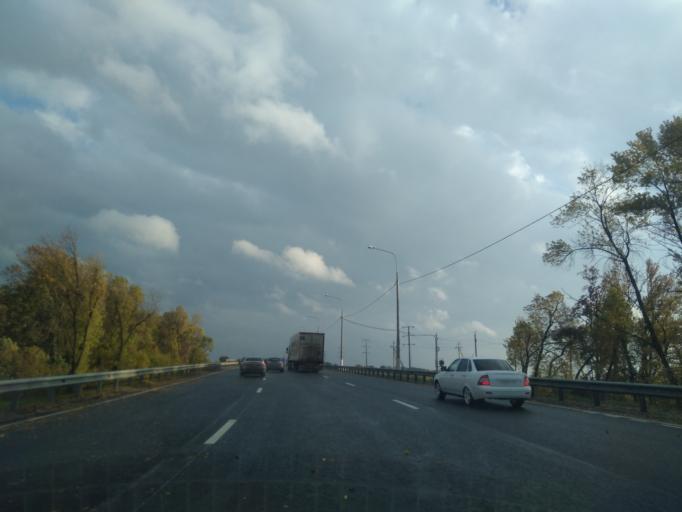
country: RU
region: Lipetsk
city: Yelets
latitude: 52.5476
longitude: 38.7152
